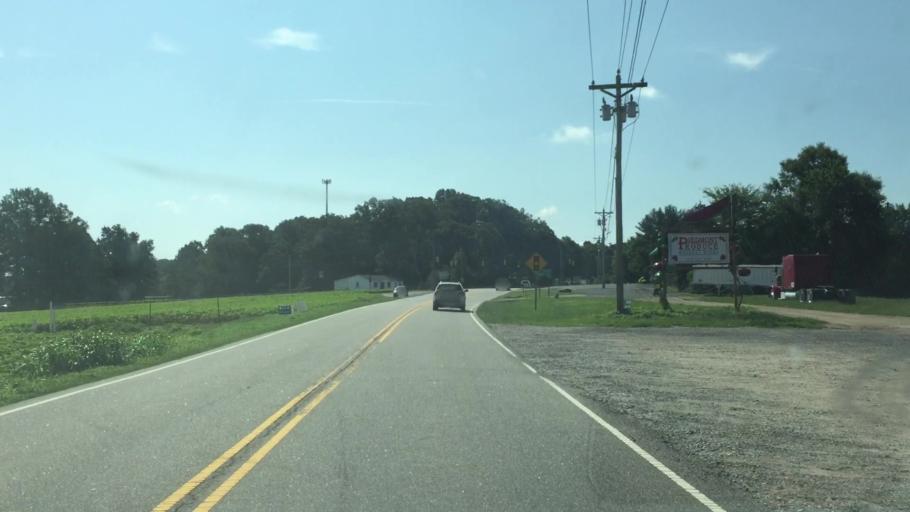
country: US
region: North Carolina
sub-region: Union County
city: Unionville
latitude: 35.1298
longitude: -80.4338
